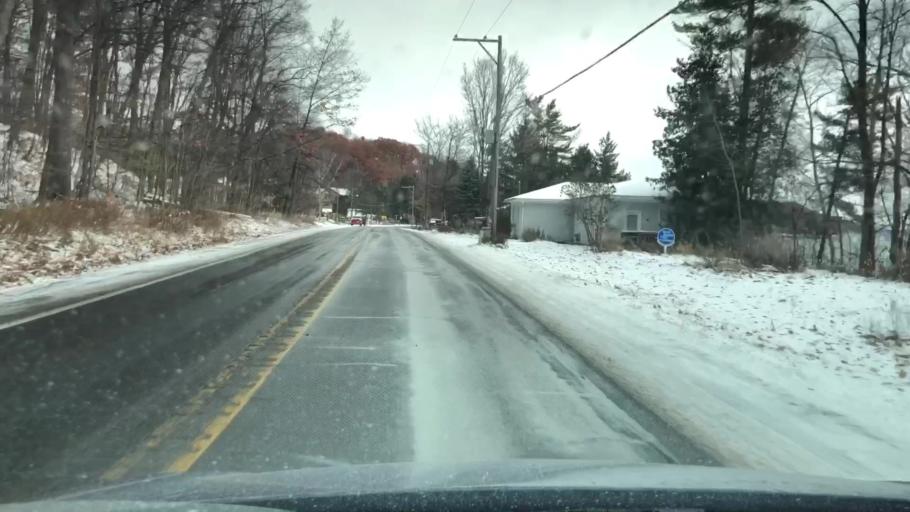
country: US
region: Michigan
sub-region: Grand Traverse County
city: Traverse City
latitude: 44.8314
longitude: -85.5432
